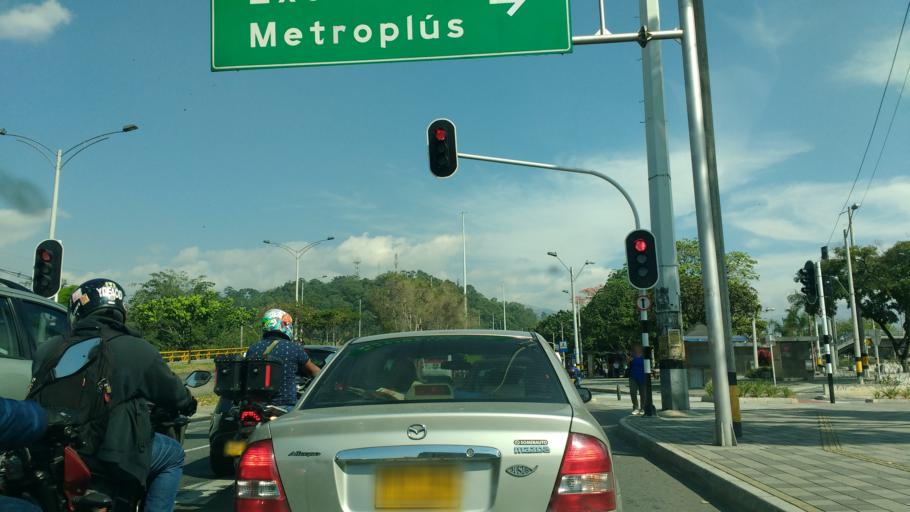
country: CO
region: Antioquia
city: Medellin
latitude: 6.2300
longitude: -75.5770
